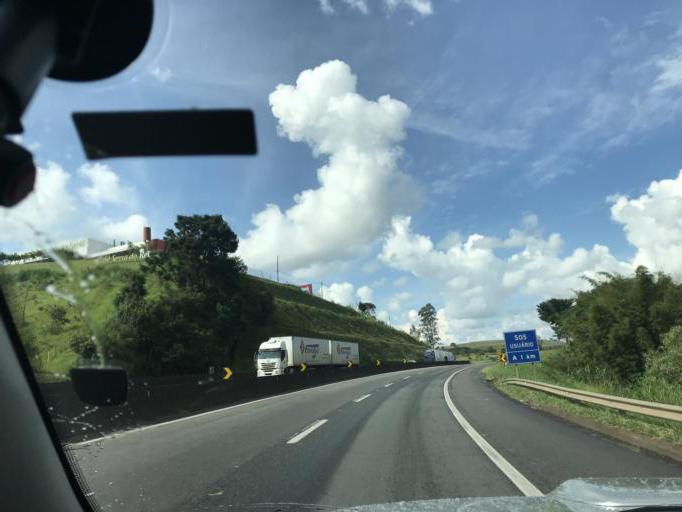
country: BR
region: Minas Gerais
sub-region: Tres Coracoes
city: Tres Coracoes
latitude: -21.6629
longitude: -45.3079
